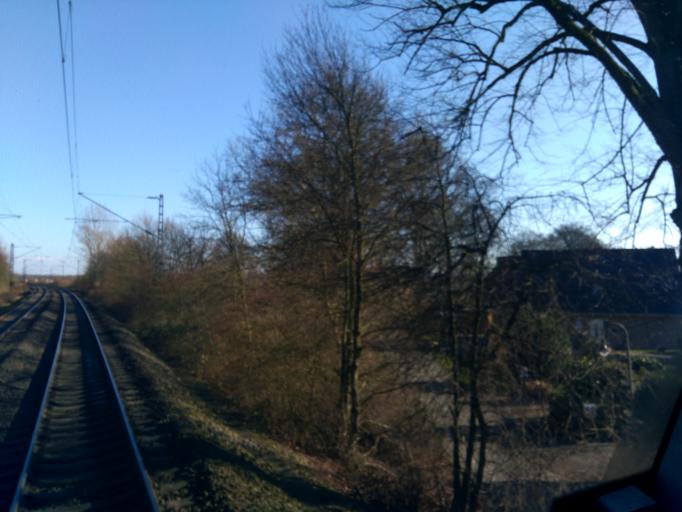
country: DE
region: Lower Saxony
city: Lilienthal
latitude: 53.0853
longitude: 8.9477
